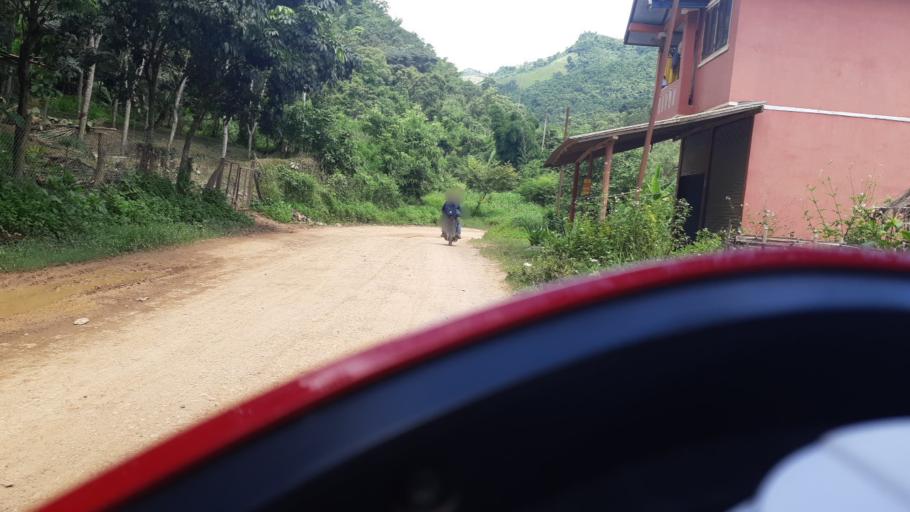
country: LA
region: Loungnamtha
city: Muang Nale
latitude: 20.1549
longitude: 101.5031
